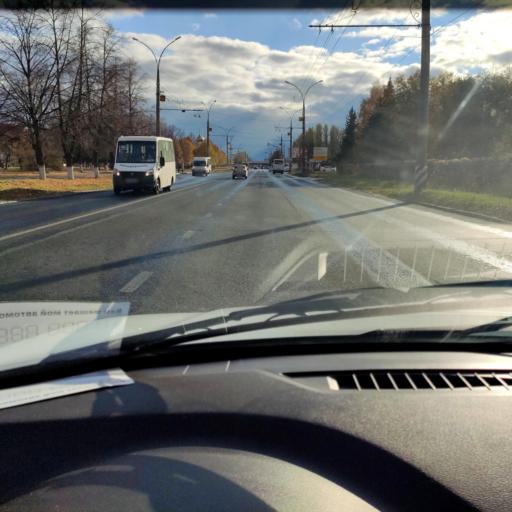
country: RU
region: Samara
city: Tol'yatti
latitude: 53.5225
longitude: 49.2746
